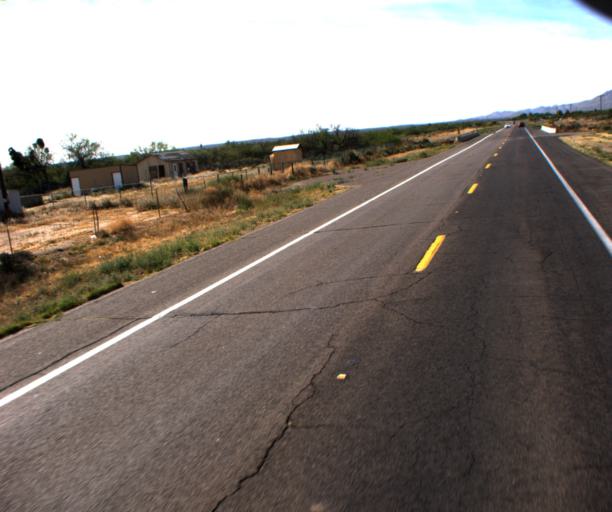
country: US
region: Arizona
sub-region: Graham County
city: Swift Trail Junction
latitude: 32.6947
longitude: -109.7078
